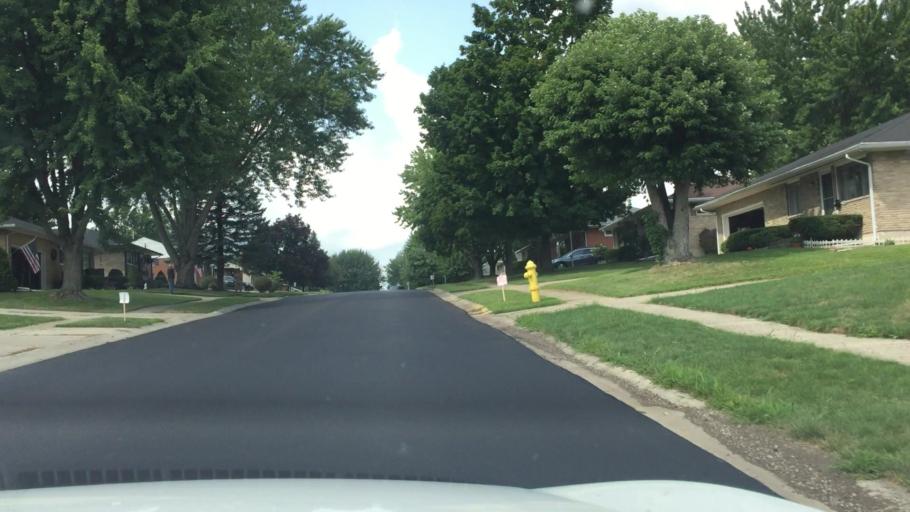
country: US
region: Ohio
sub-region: Clark County
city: Northridge
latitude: 39.9845
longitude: -83.7791
